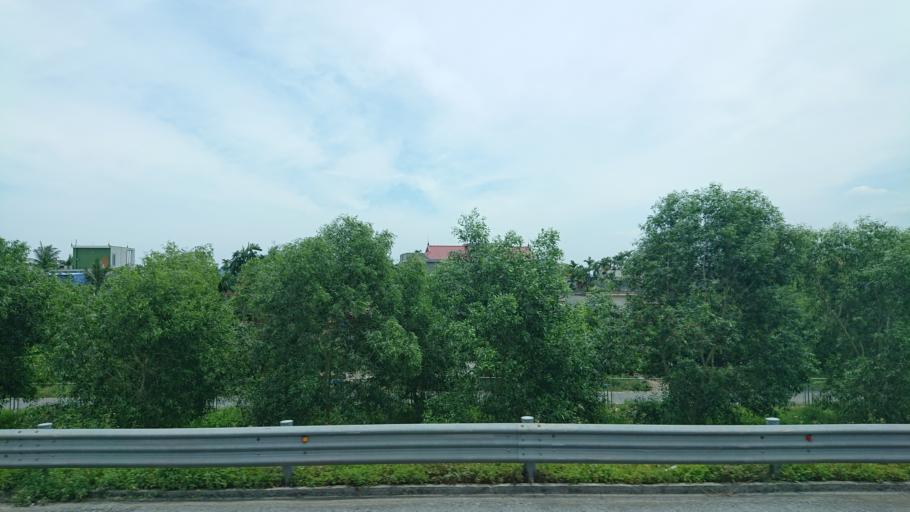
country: VN
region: Hai Phong
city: Nui Doi
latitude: 20.7682
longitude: 106.6349
